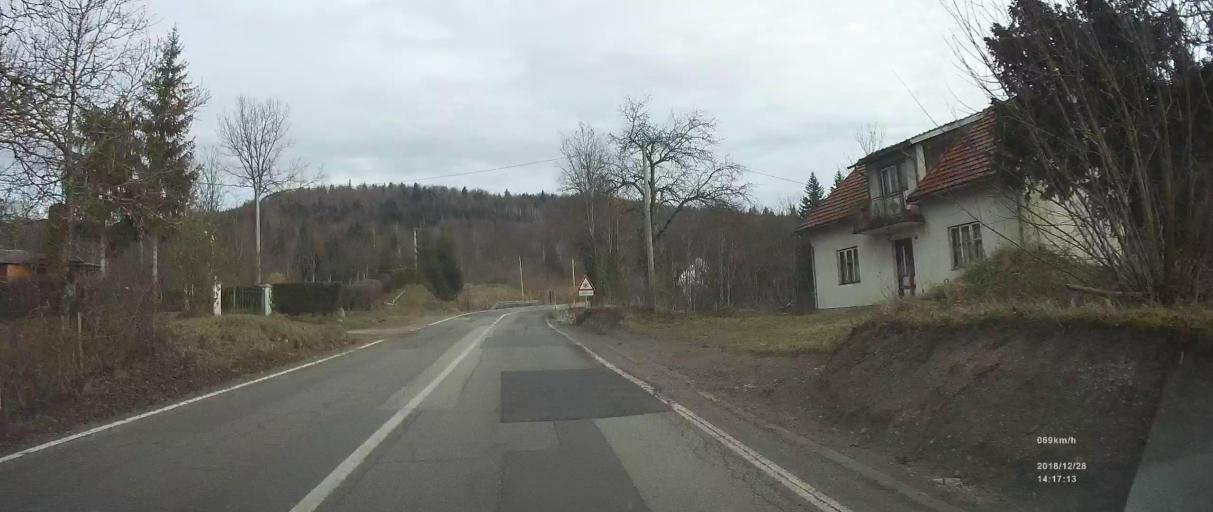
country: HR
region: Primorsko-Goranska
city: Vrbovsko
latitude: 45.4185
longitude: 15.0457
